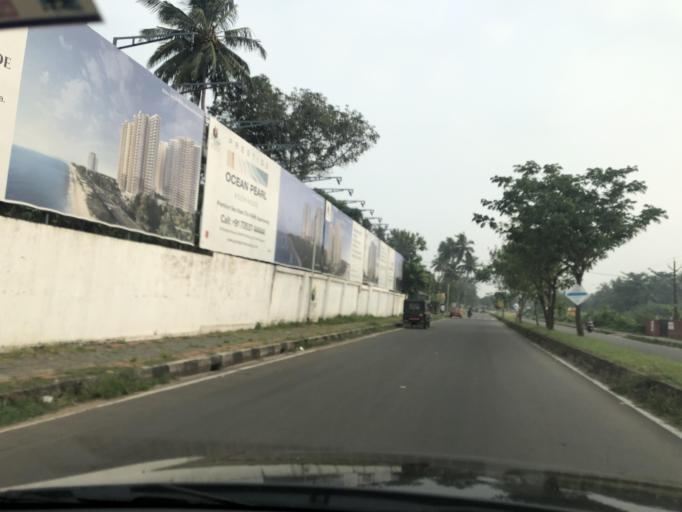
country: IN
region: Kerala
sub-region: Kozhikode
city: Kozhikode
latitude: 11.2883
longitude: 75.7595
